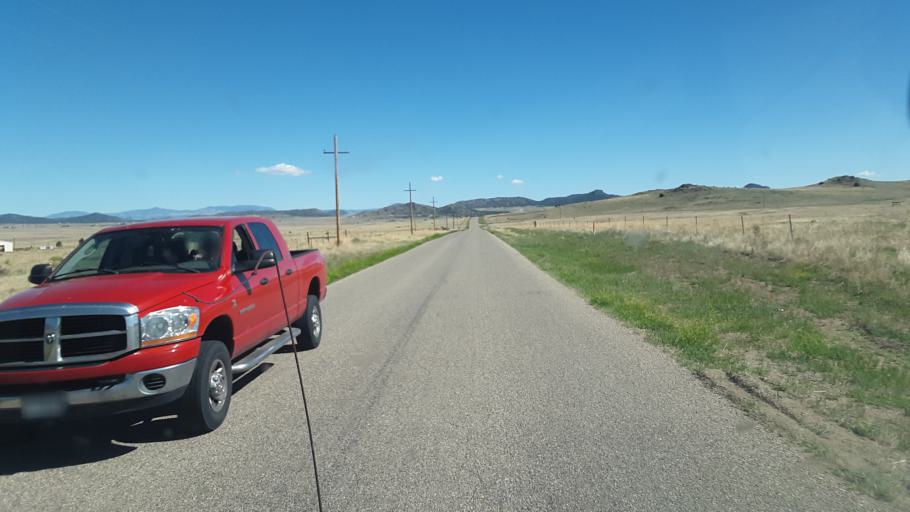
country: US
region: Colorado
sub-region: Custer County
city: Westcliffe
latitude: 38.1722
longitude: -105.4617
